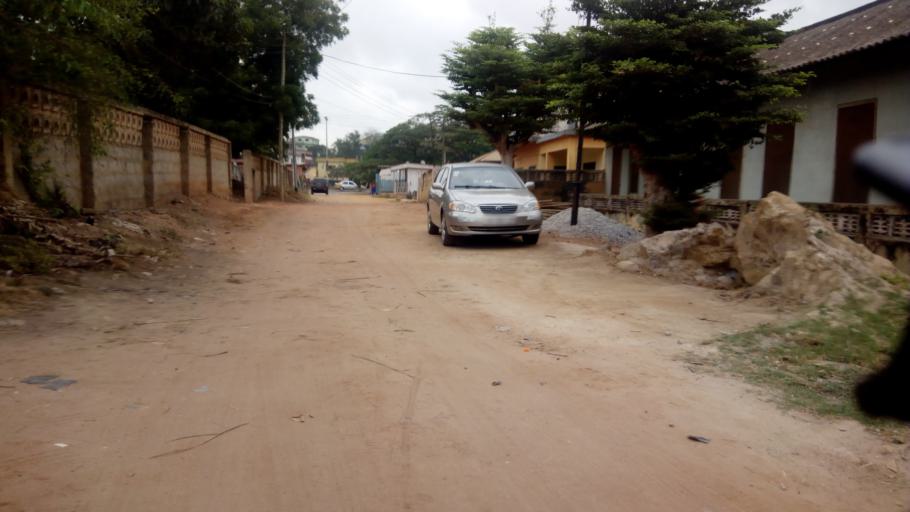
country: GH
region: Central
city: Cape Coast
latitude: 5.1200
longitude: -1.2686
